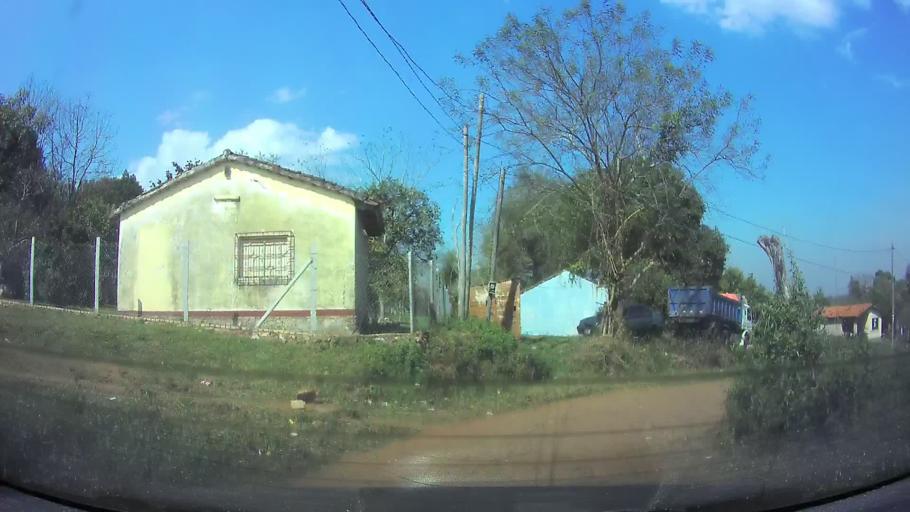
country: PY
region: Central
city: Limpio
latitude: -25.2340
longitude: -57.4412
